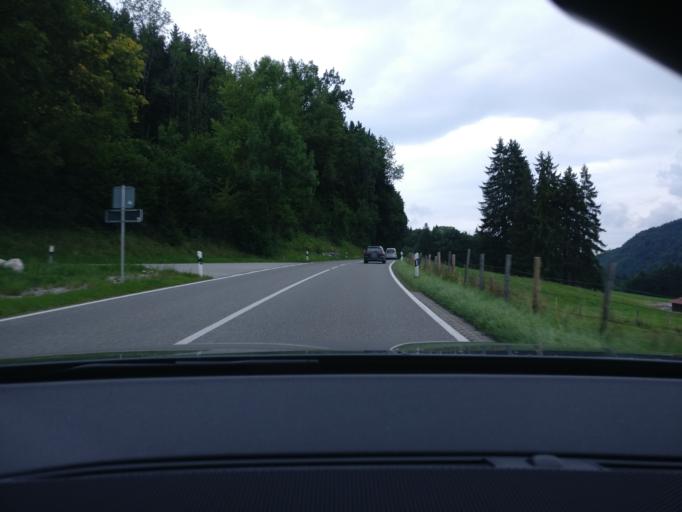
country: DE
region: Bavaria
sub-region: Upper Bavaria
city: Rottenbuch
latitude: 47.7556
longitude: 10.9402
